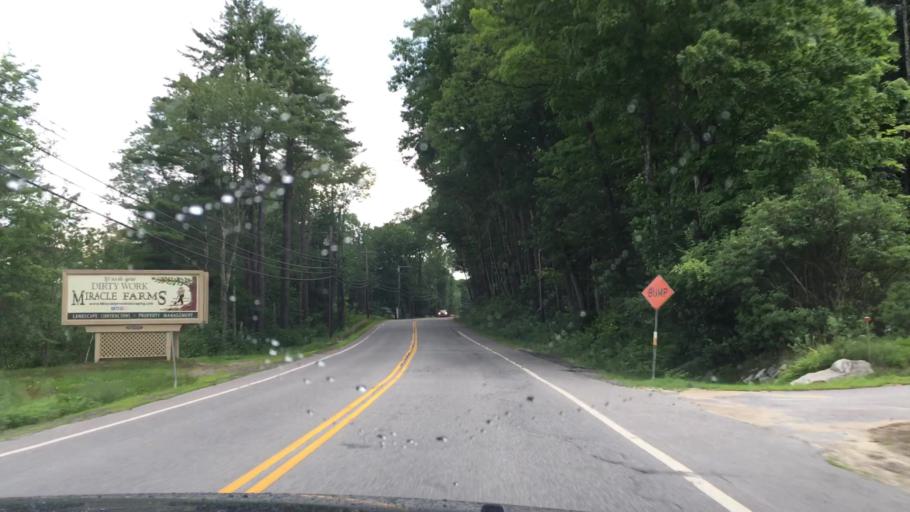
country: US
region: New Hampshire
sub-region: Belknap County
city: Meredith
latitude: 43.6773
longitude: -71.5078
